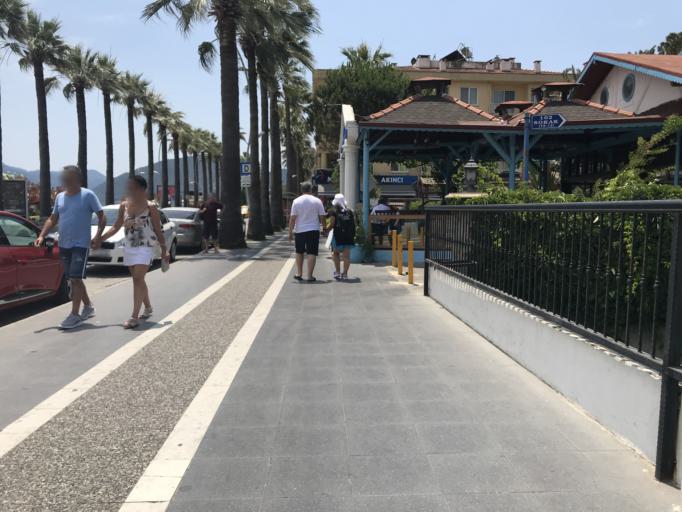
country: TR
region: Mugla
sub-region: Marmaris
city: Marmaris
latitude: 36.8521
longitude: 28.2666
